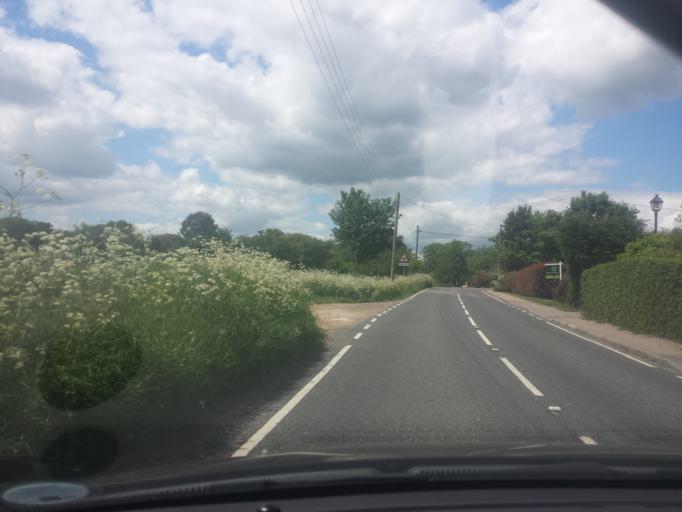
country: GB
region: England
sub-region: Essex
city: Little Clacton
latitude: 51.8804
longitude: 1.1658
